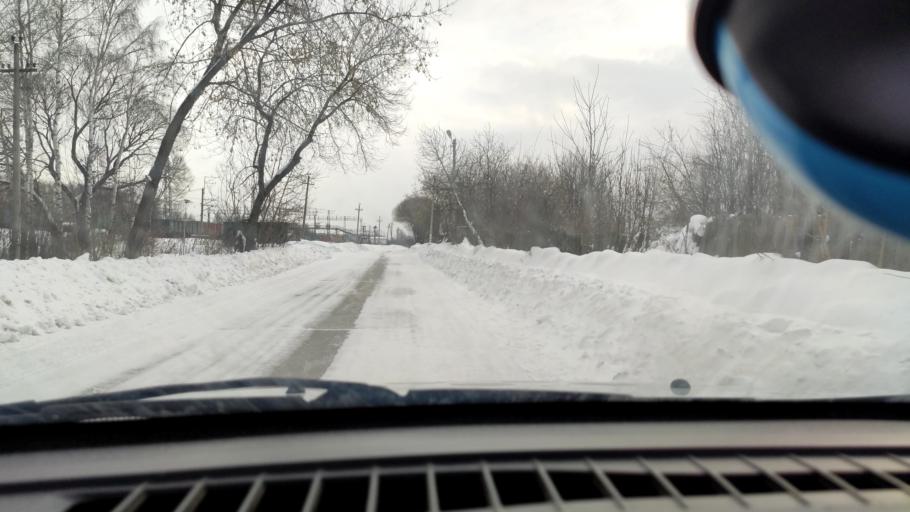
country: RU
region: Perm
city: Overyata
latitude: 58.0879
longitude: 55.8649
